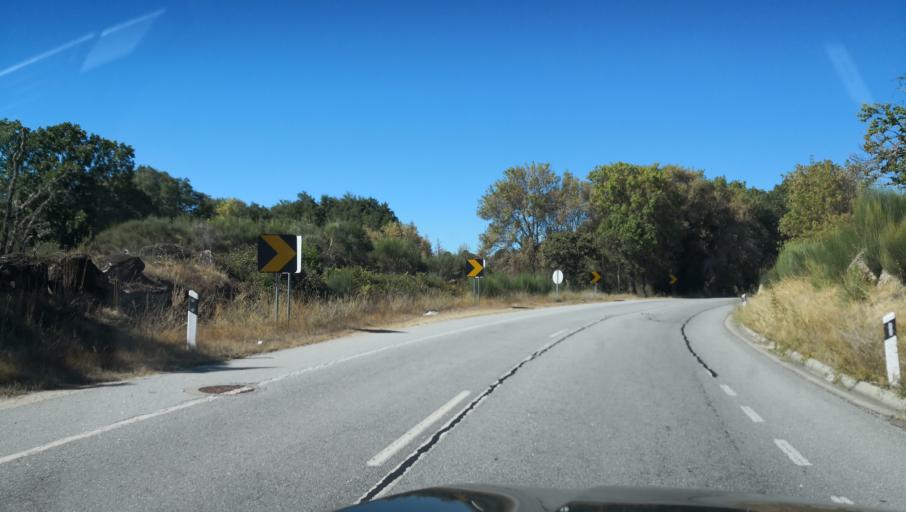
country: PT
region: Vila Real
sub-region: Valpacos
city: Valpacos
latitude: 41.6447
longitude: -7.3196
